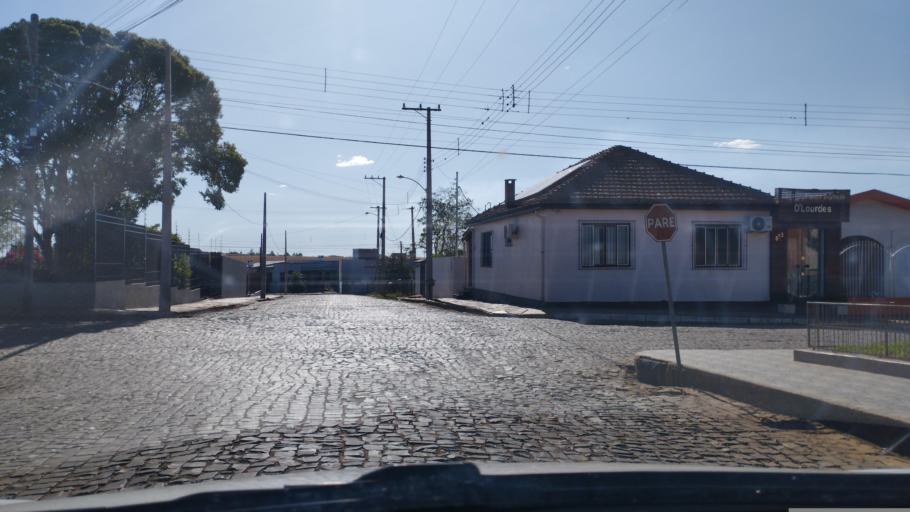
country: BR
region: Rio Grande do Sul
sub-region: Tupancireta
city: Tupancireta
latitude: -29.0858
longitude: -53.8381
